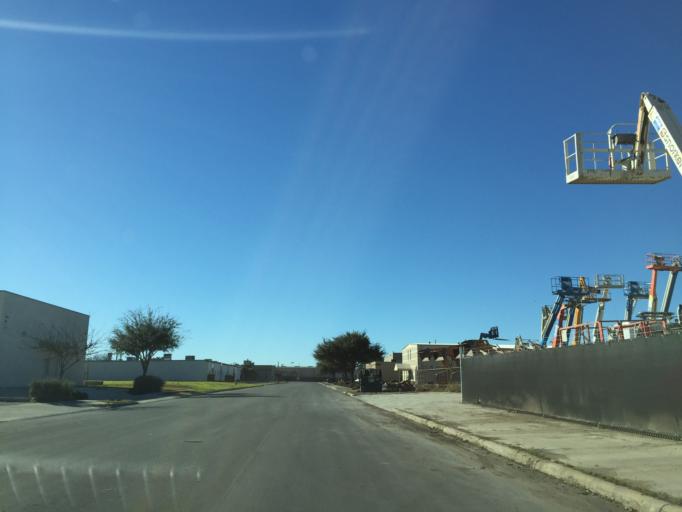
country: US
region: Texas
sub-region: Bexar County
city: Castle Hills
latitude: 29.5523
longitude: -98.4890
